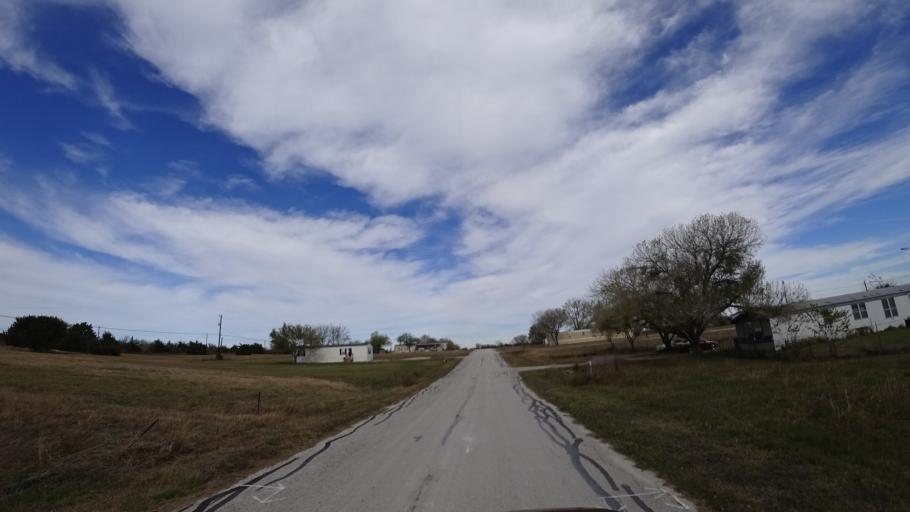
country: US
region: Texas
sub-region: Travis County
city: Onion Creek
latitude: 30.1146
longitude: -97.7295
